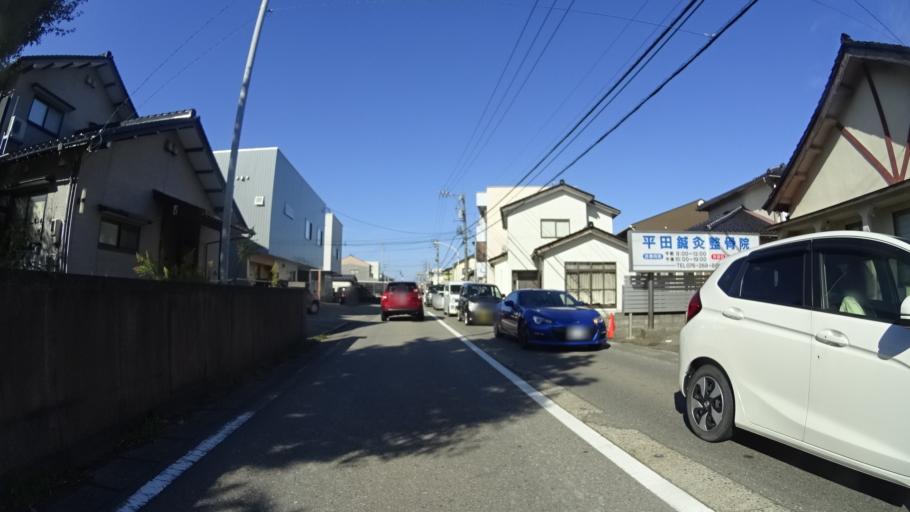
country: JP
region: Ishikawa
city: Kanazawa-shi
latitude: 36.5926
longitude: 136.6104
